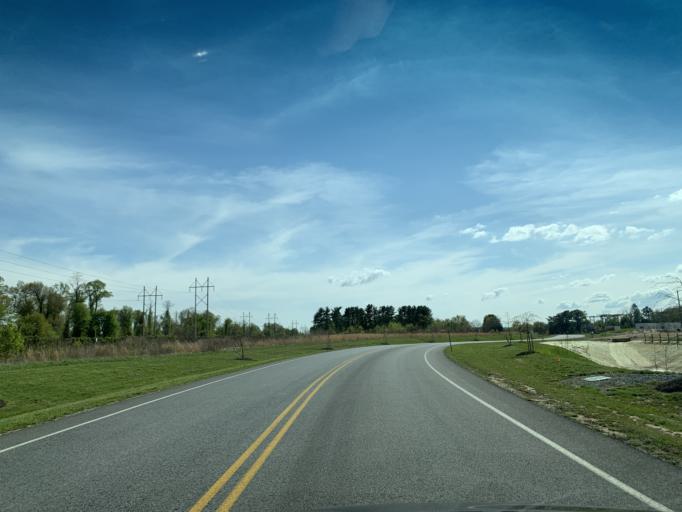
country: US
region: Maryland
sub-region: Harford County
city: Perryman
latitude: 39.4672
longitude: -76.1938
